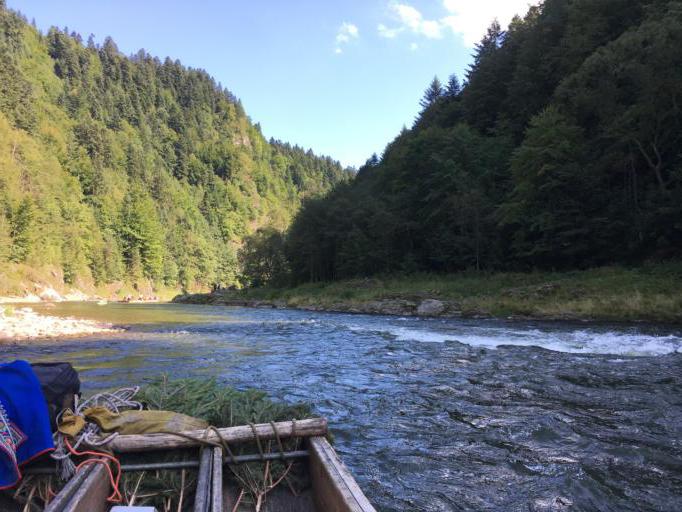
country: PL
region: Lesser Poland Voivodeship
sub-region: Powiat nowotarski
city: Kroscienko nad Dunajcem
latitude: 49.4032
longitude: 20.4253
